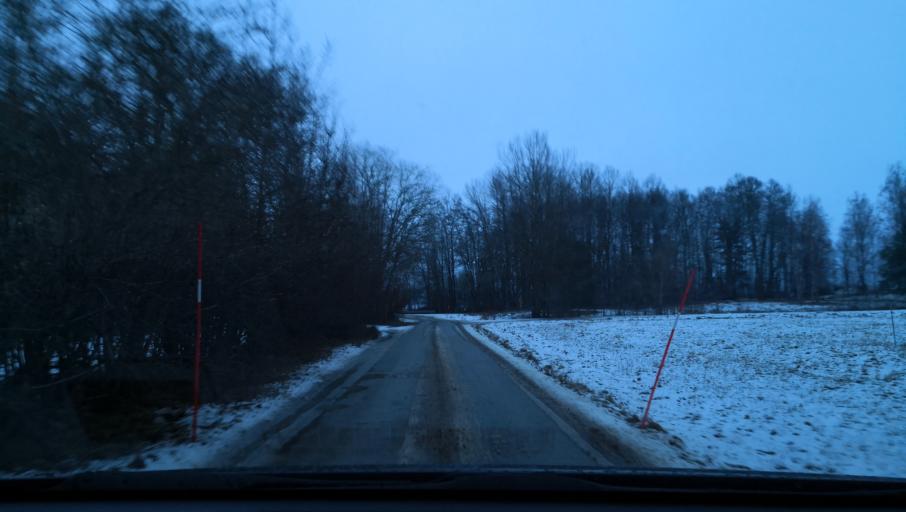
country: SE
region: Vaestmanland
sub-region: Kungsors Kommun
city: Kungsoer
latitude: 59.3967
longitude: 16.2062
